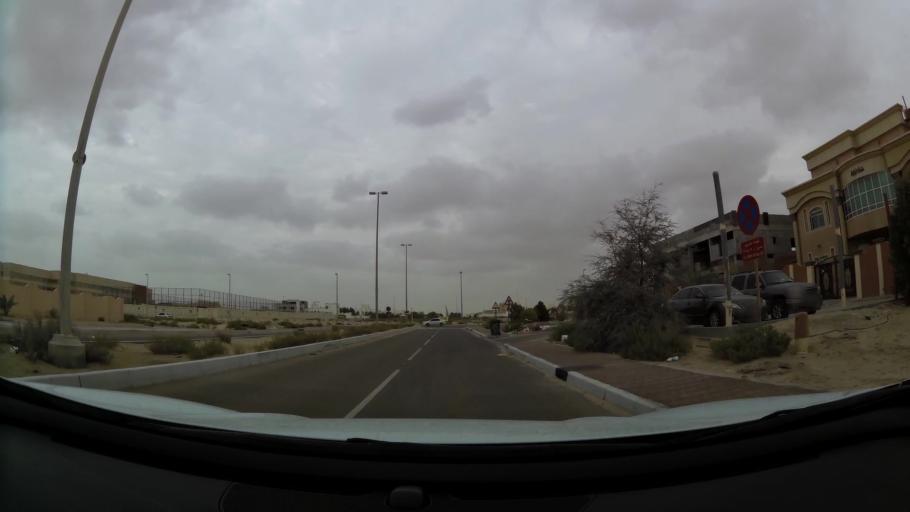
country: AE
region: Abu Dhabi
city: Abu Dhabi
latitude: 24.3881
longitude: 54.6549
